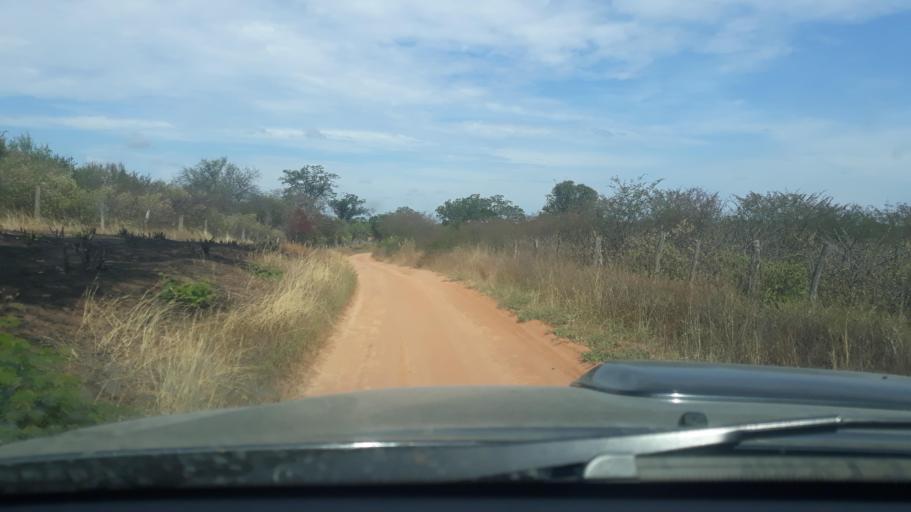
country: BR
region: Bahia
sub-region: Riacho De Santana
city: Riacho de Santana
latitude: -13.8552
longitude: -43.0588
